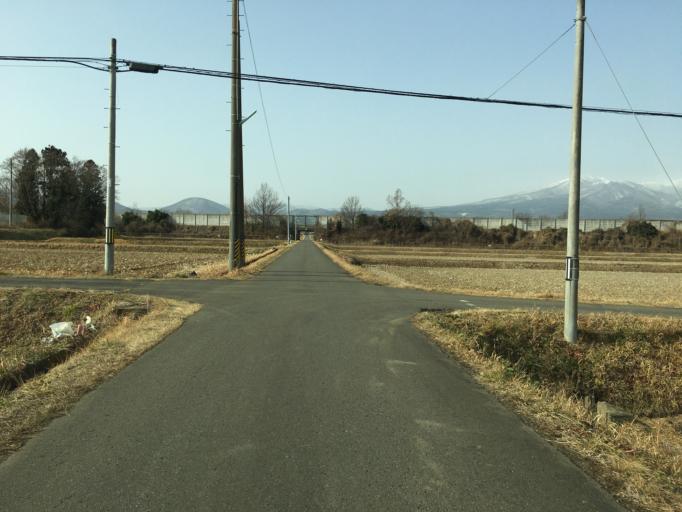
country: JP
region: Fukushima
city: Motomiya
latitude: 37.5349
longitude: 140.3872
